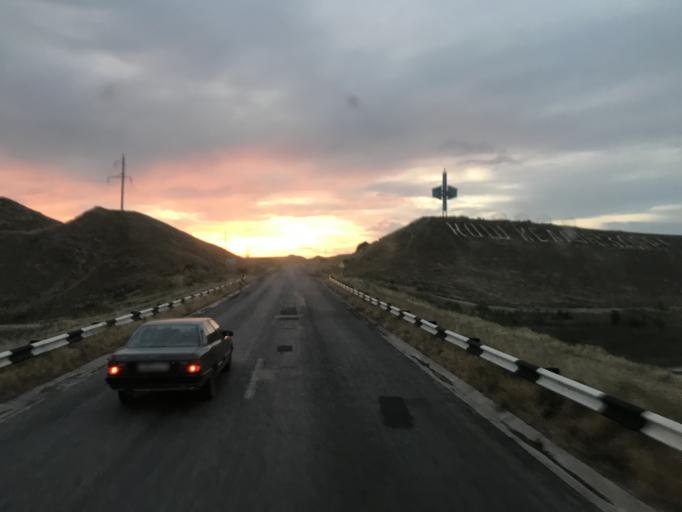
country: KZ
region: Ongtustik Qazaqstan
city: Ilyich
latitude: 41.0539
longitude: 68.5771
